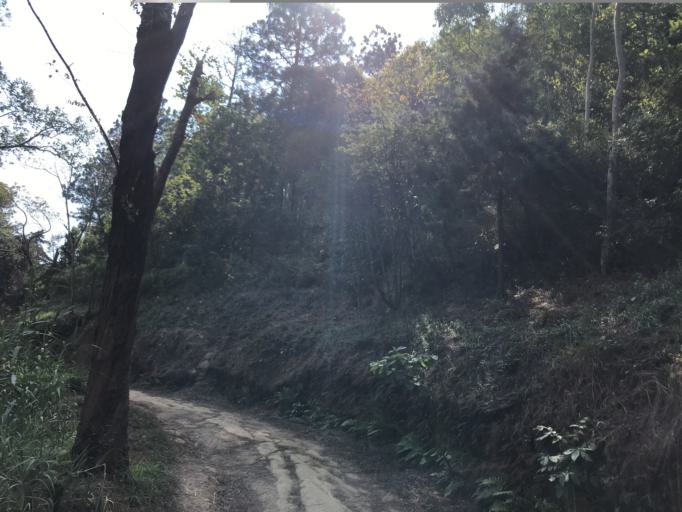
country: GT
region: Guatemala
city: Petapa
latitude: 14.4830
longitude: -90.5524
